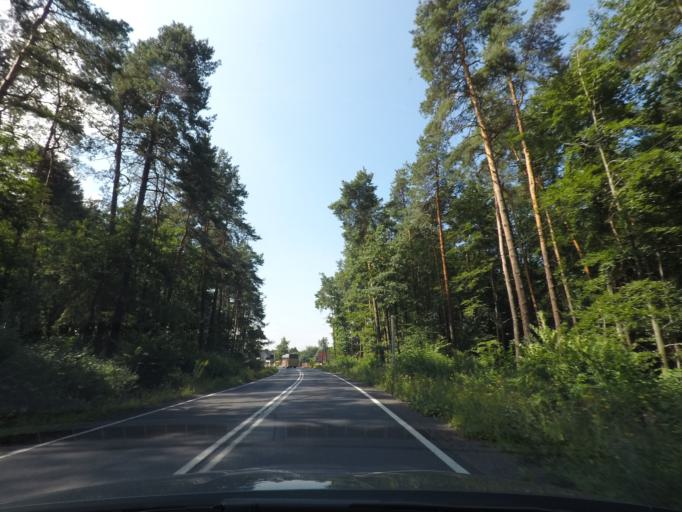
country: PL
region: Lesser Poland Voivodeship
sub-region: Powiat chrzanowski
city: Libiaz
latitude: 50.0895
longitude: 19.2899
